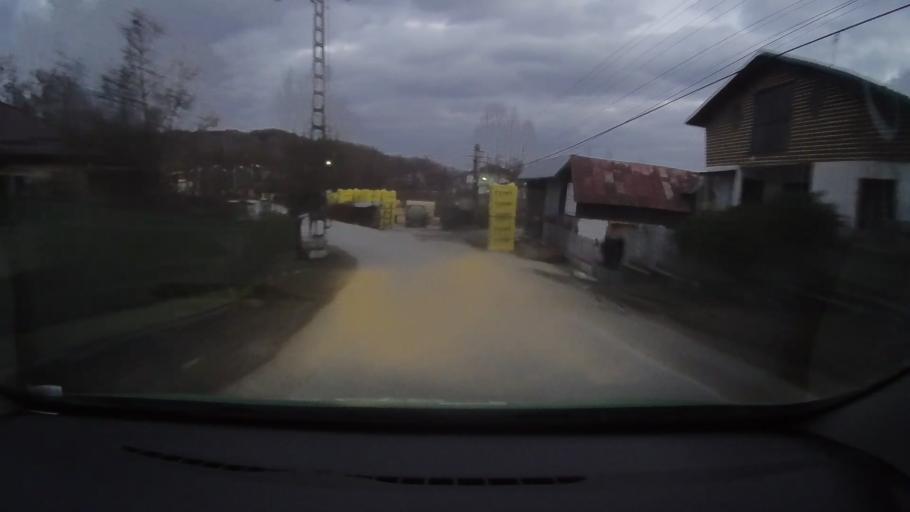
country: RO
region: Prahova
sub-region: Comuna Provita de Sus
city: Provita de Sus
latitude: 45.1381
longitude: 25.6327
